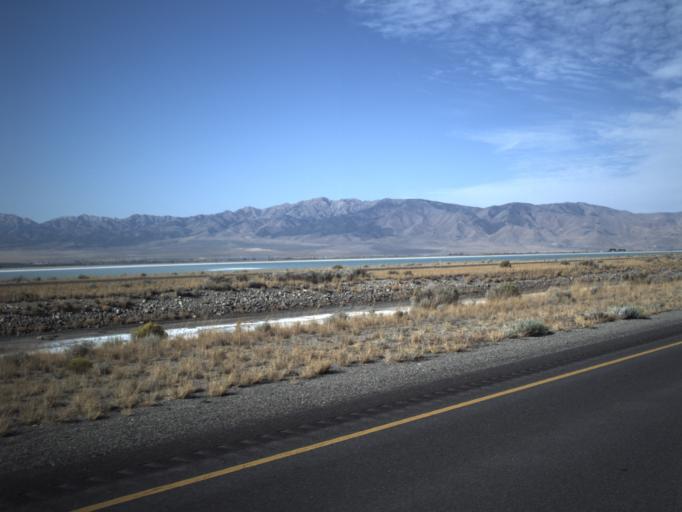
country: US
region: Utah
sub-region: Tooele County
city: Stansbury park
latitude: 40.6666
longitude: -112.3699
